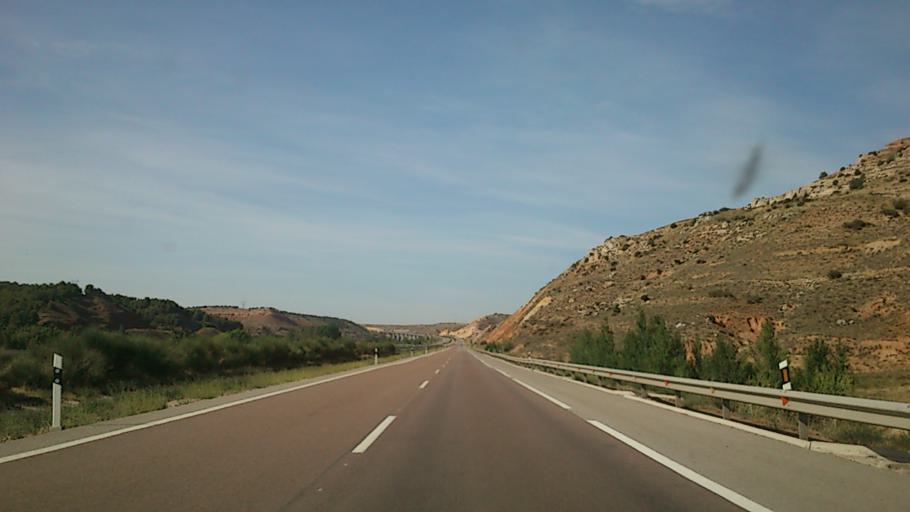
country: ES
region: Aragon
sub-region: Provincia de Teruel
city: Calamocha
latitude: 40.9726
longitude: -1.2600
